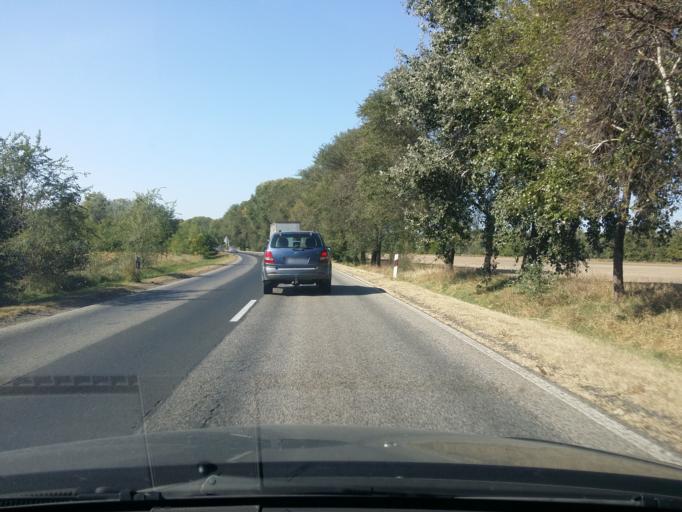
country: HU
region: Bacs-Kiskun
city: Nyarlorinc
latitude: 46.9151
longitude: 19.7990
